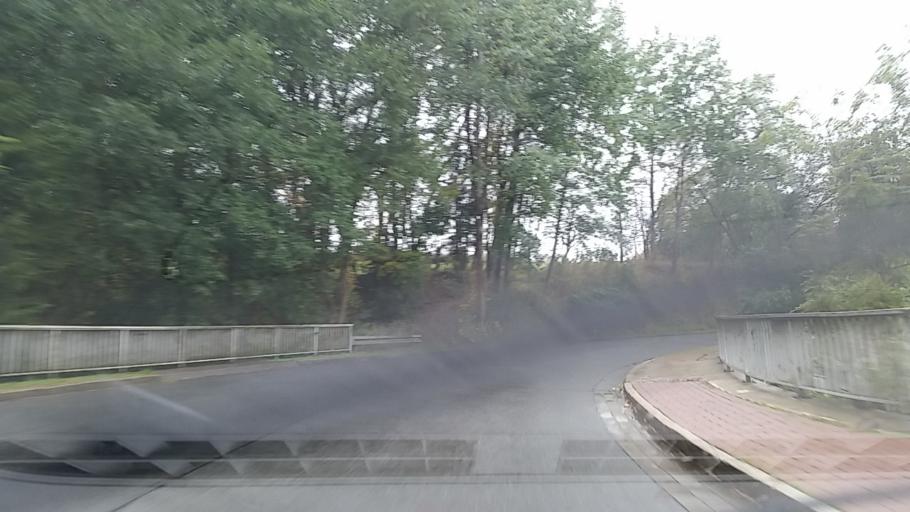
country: DE
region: Lower Saxony
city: Altenau
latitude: 51.7955
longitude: 10.4518
